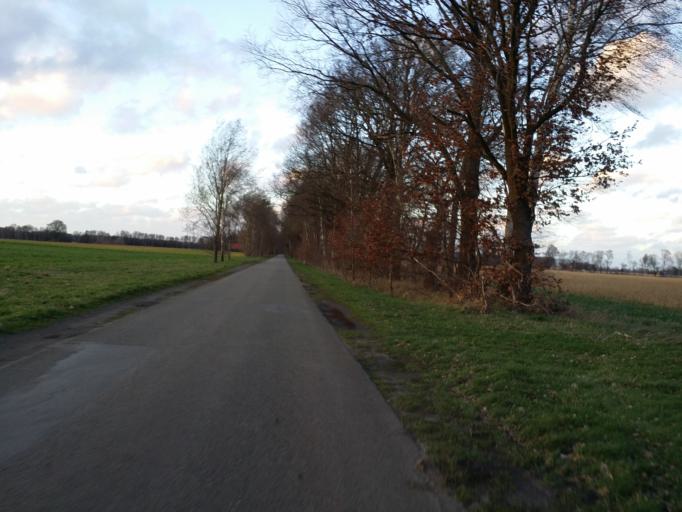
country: DE
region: Lower Saxony
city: Gross Ippener
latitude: 52.9857
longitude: 8.5995
